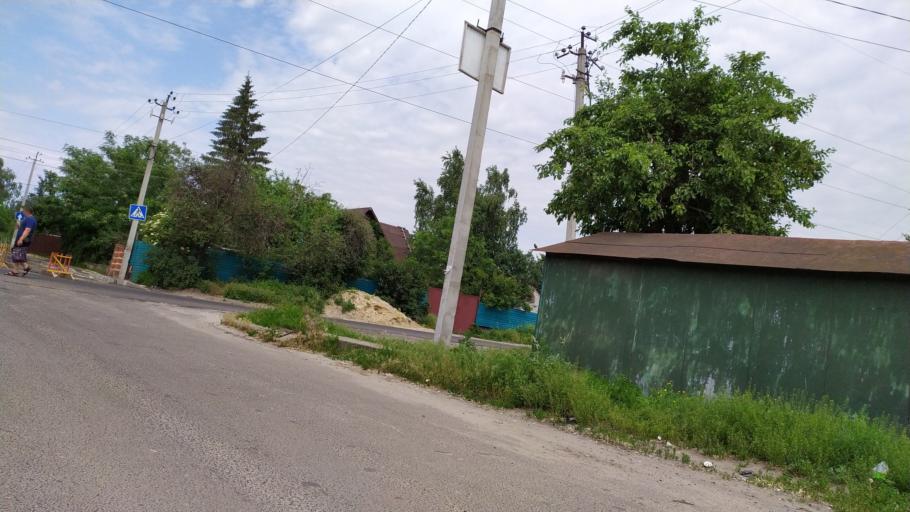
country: RU
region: Kursk
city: Kursk
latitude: 51.6644
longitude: 36.1507
